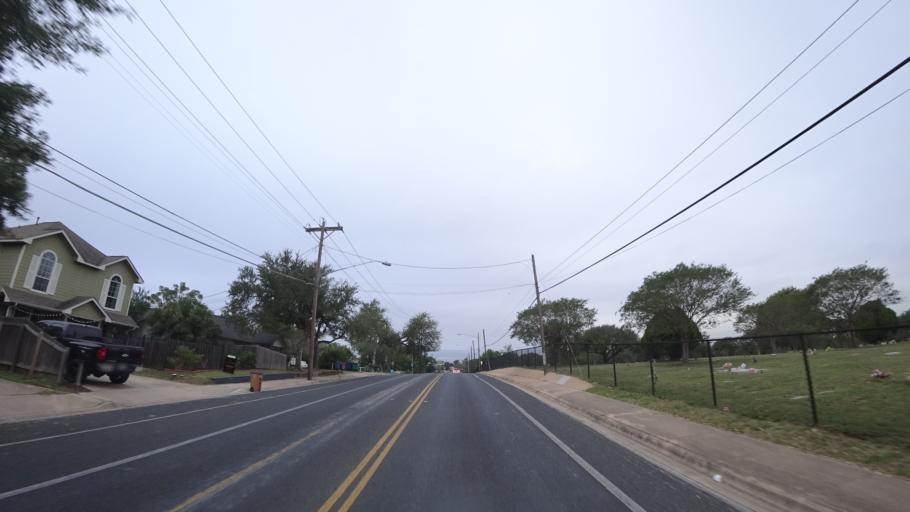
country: US
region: Texas
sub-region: Travis County
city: Austin
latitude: 30.2773
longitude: -97.6978
